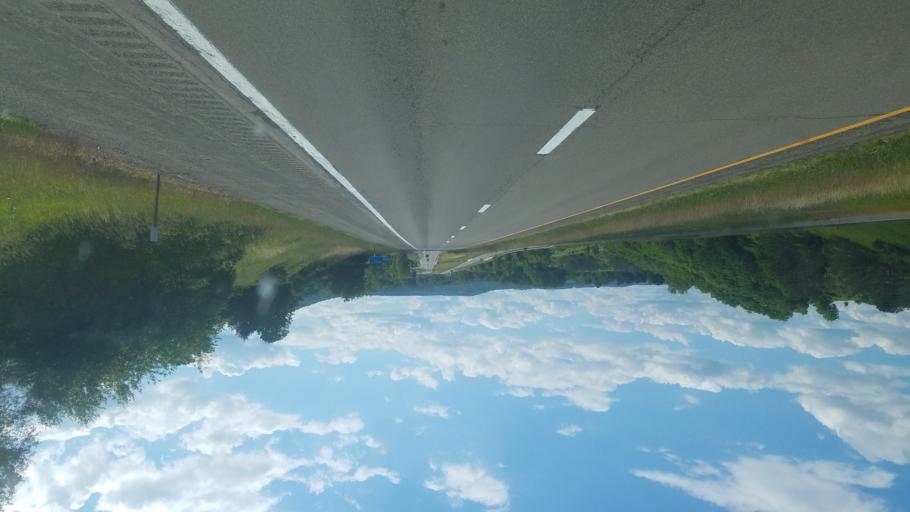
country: US
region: New York
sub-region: Steuben County
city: Hornell
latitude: 42.3297
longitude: -77.7373
